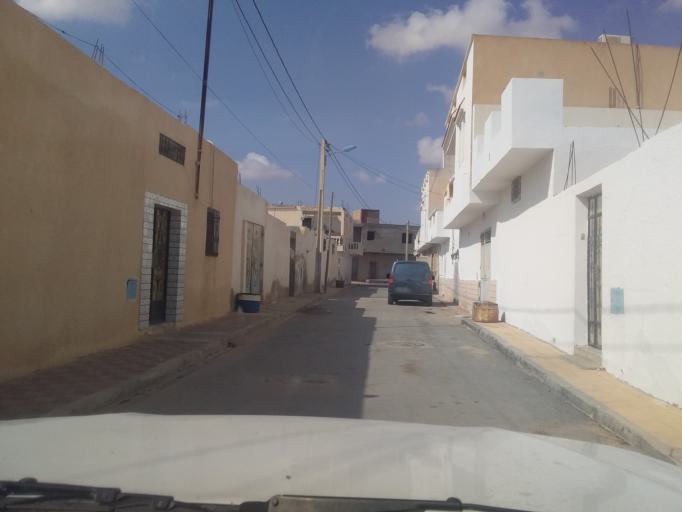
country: TN
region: Qabis
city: Gabes
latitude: 33.6219
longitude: 10.2811
